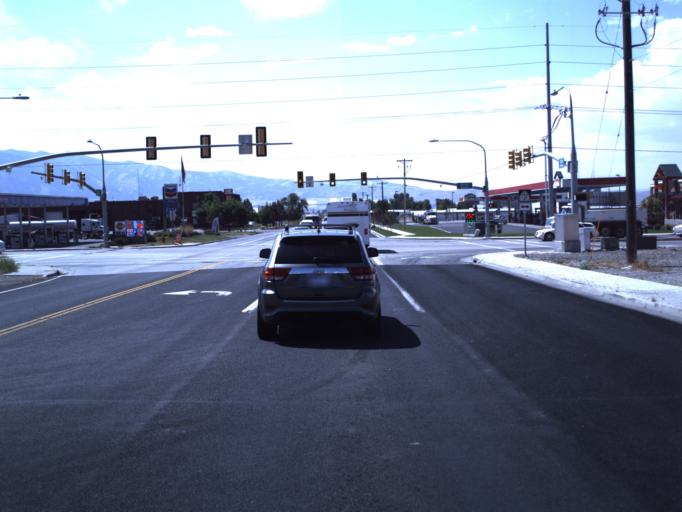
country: US
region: Utah
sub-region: Cache County
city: Logan
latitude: 41.7357
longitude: -111.8588
